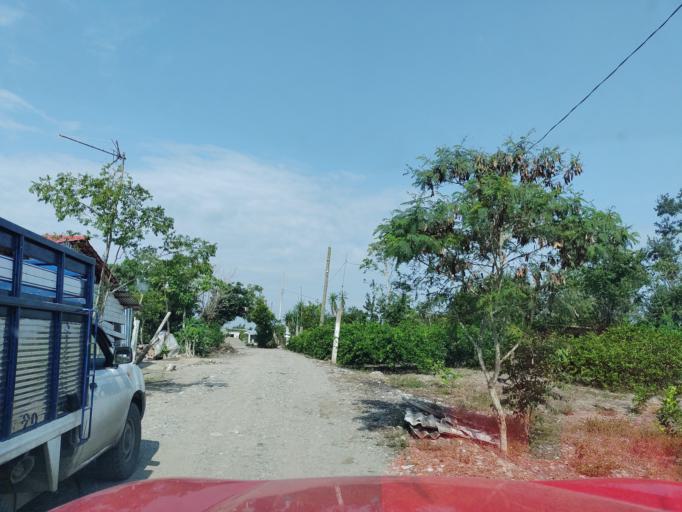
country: MX
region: Puebla
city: Espinal
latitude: 20.2751
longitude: -97.3319
